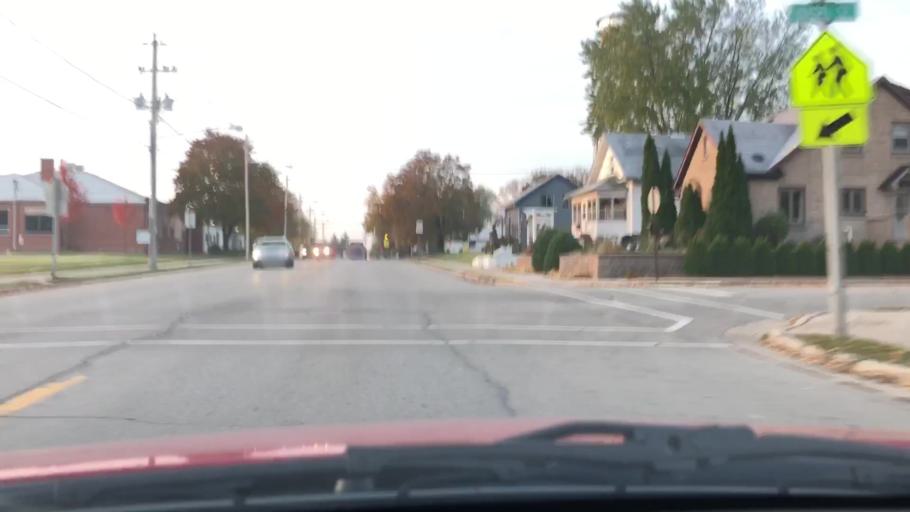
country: US
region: Wisconsin
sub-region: Outagamie County
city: Seymour
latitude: 44.5029
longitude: -88.3307
